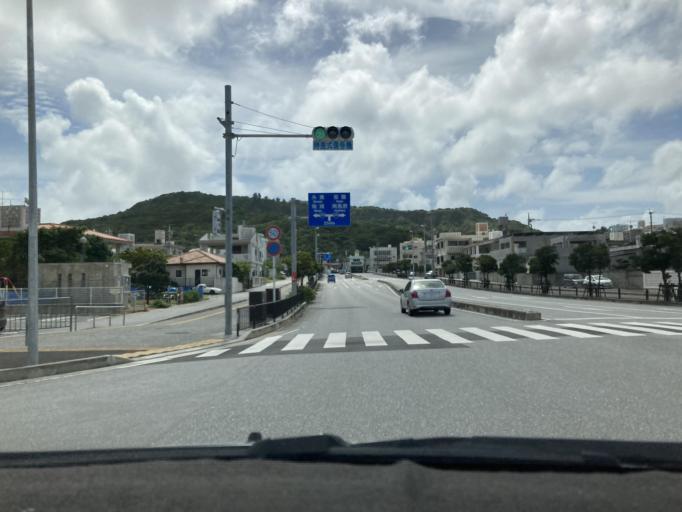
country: JP
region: Okinawa
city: Ginowan
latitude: 26.2022
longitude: 127.7605
